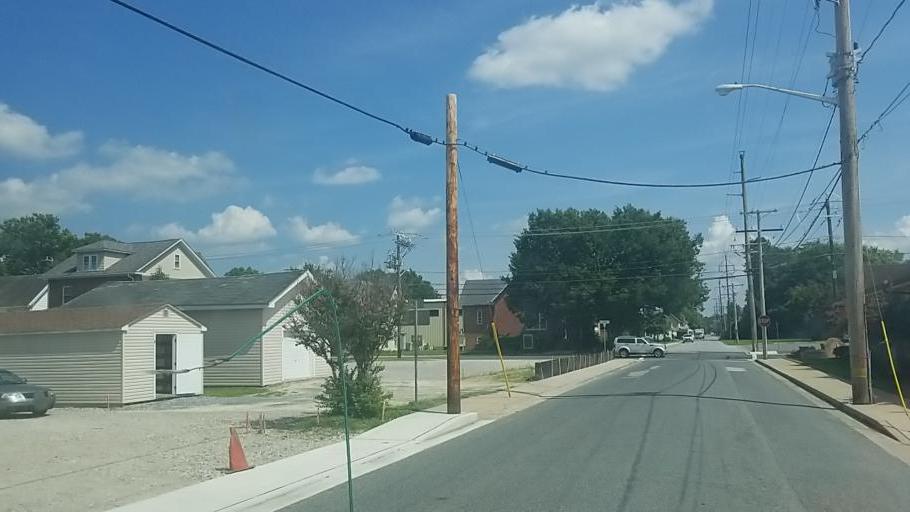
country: US
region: Maryland
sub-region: Wicomico County
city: Hebron
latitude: 38.4197
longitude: -75.6892
